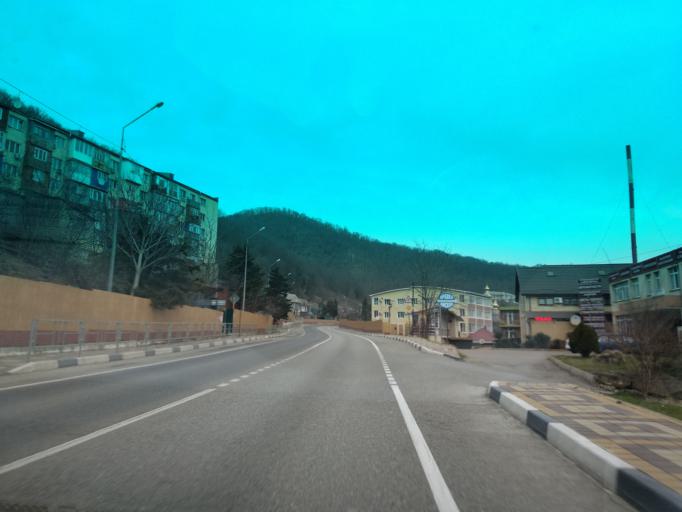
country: RU
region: Krasnodarskiy
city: Ol'ginka
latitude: 44.2012
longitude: 38.8873
